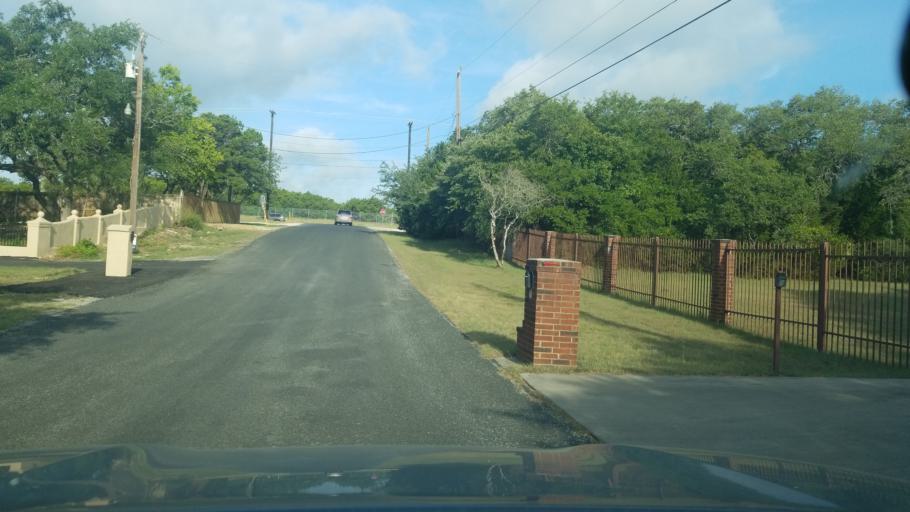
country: US
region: Texas
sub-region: Bexar County
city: Timberwood Park
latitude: 29.6955
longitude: -98.5204
